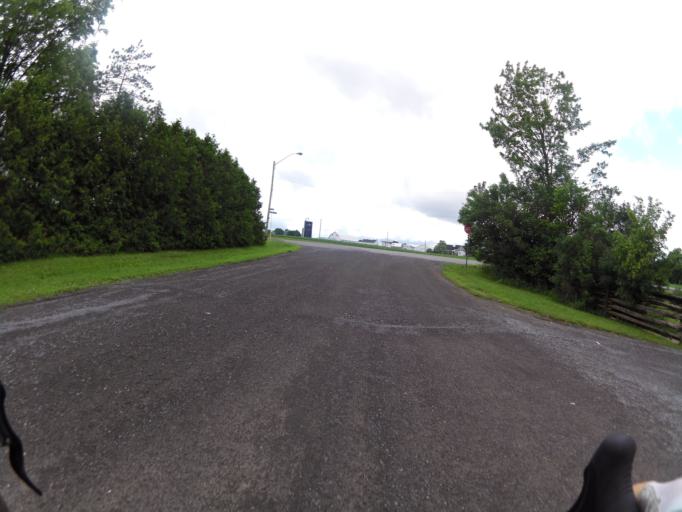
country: CA
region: Ontario
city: Bells Corners
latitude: 45.2545
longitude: -75.8747
